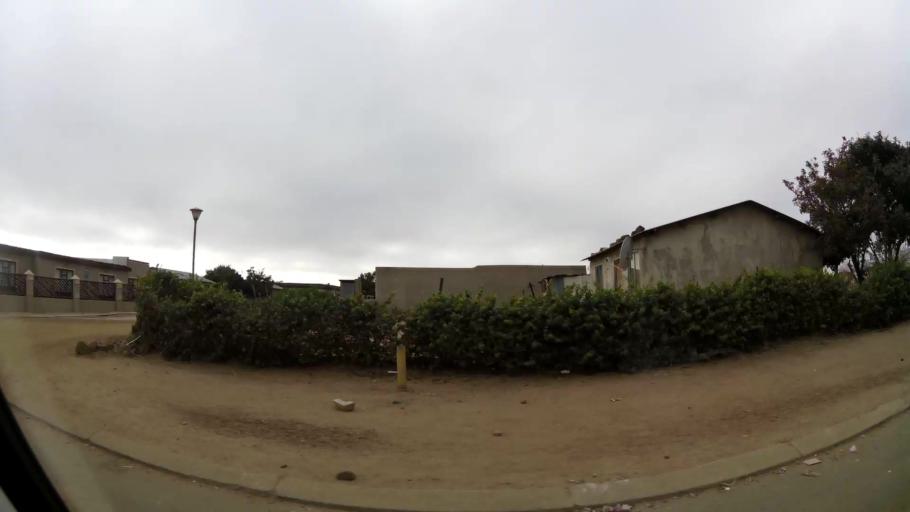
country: ZA
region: Limpopo
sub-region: Capricorn District Municipality
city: Polokwane
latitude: -23.8382
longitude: 29.3890
